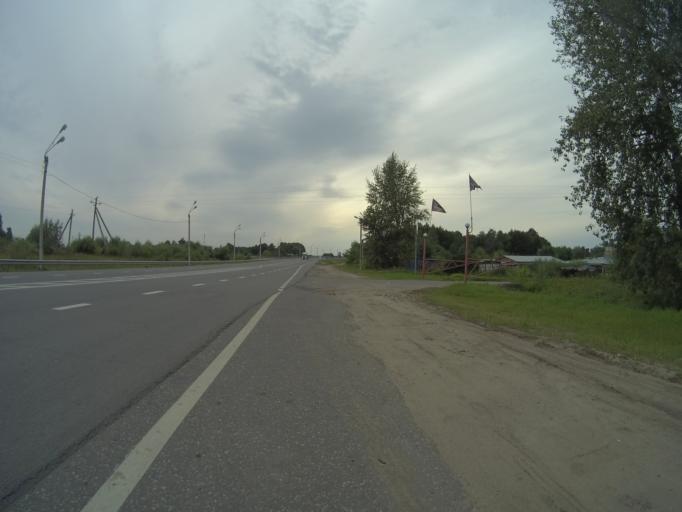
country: RU
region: Vladimir
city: Orgtrud
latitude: 56.2100
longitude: 40.5963
